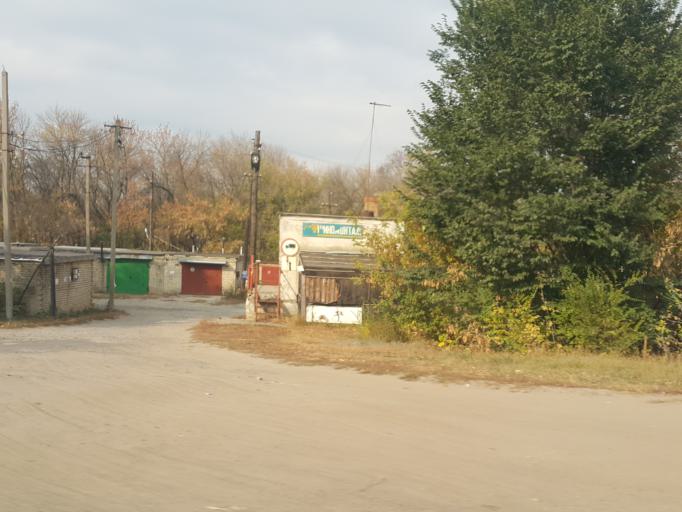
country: RU
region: Tambov
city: Bokino
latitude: 52.6665
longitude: 41.4507
